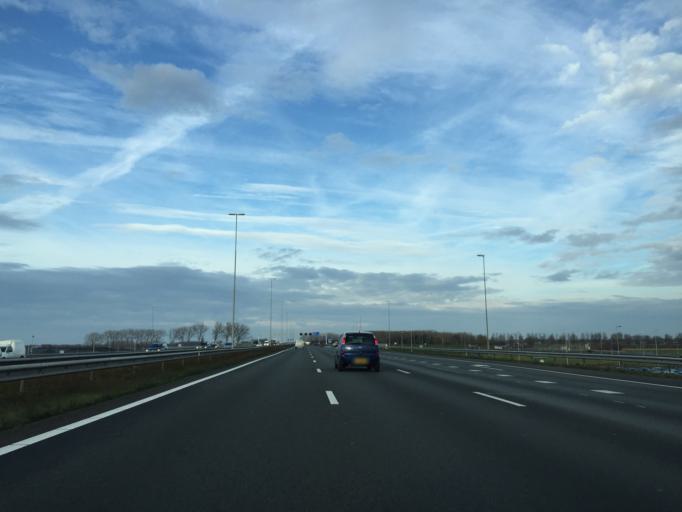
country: NL
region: Gelderland
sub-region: Gemeente Maasdriel
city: Hedel
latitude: 51.7559
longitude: 5.2857
